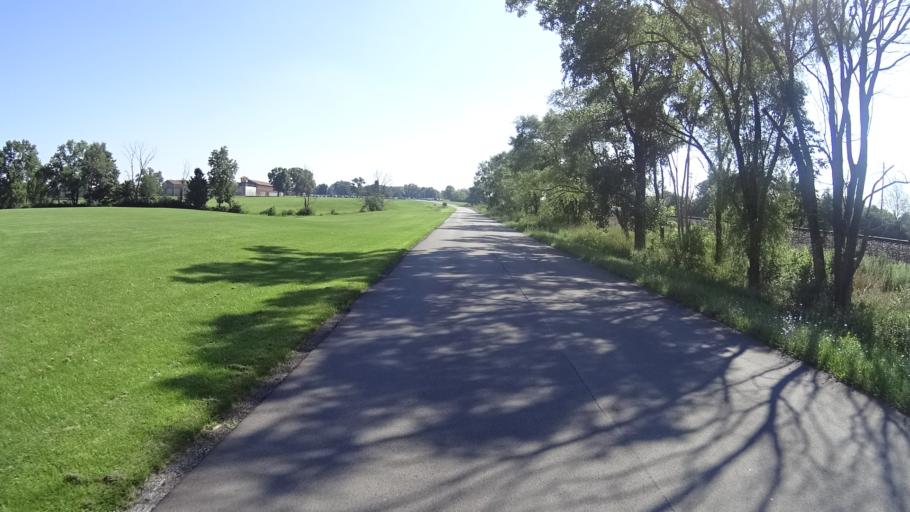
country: US
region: Indiana
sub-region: Madison County
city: Pendleton
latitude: 39.9782
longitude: -85.7629
